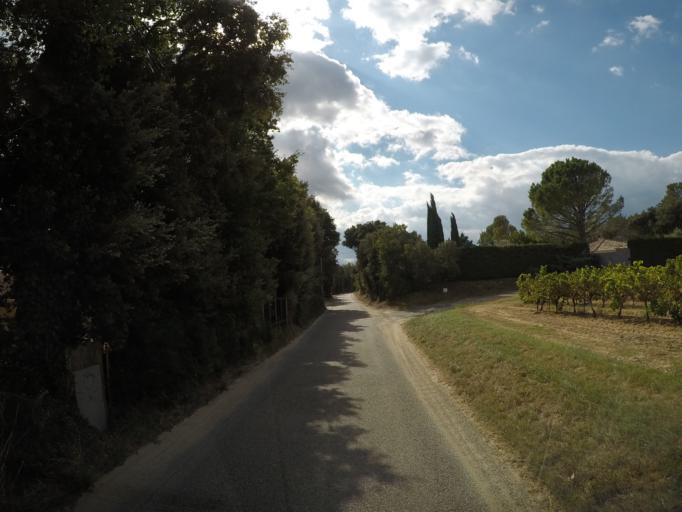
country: FR
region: Rhone-Alpes
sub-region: Departement de la Drome
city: Suze-la-Rousse
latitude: 44.2917
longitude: 4.8111
